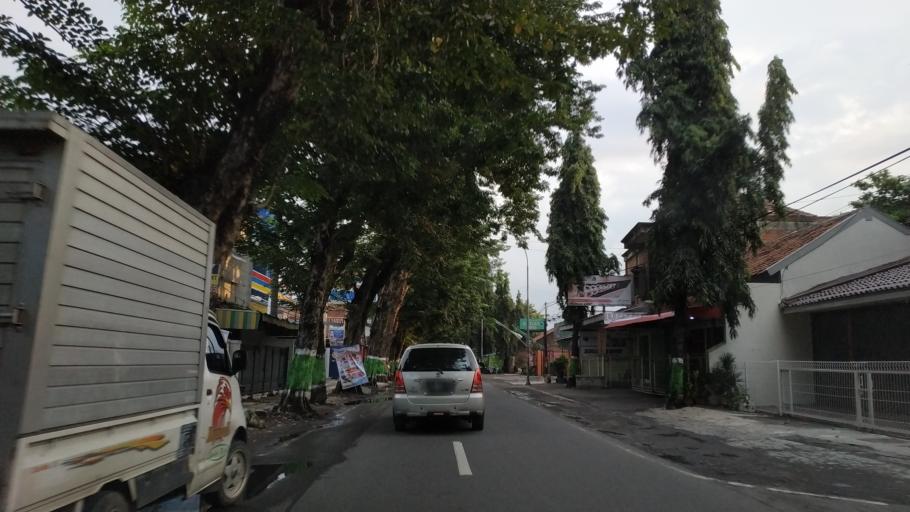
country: ID
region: Central Java
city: Kudus
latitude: -6.8054
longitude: 110.8565
